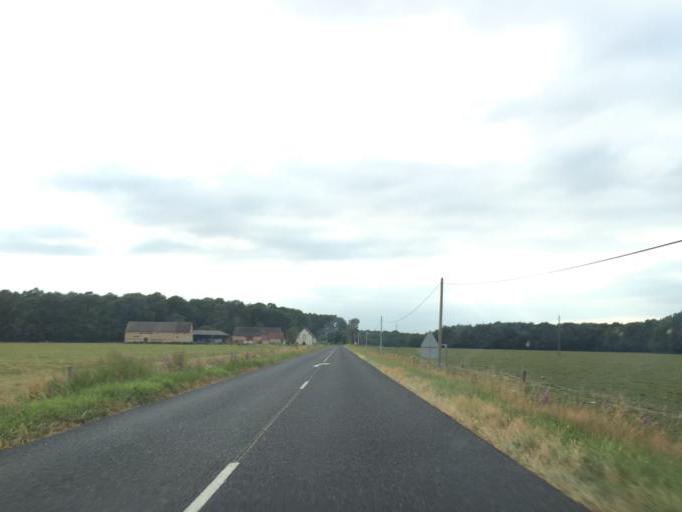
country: FR
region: Auvergne
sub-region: Departement de l'Allier
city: Lusigny
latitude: 46.5309
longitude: 3.4580
